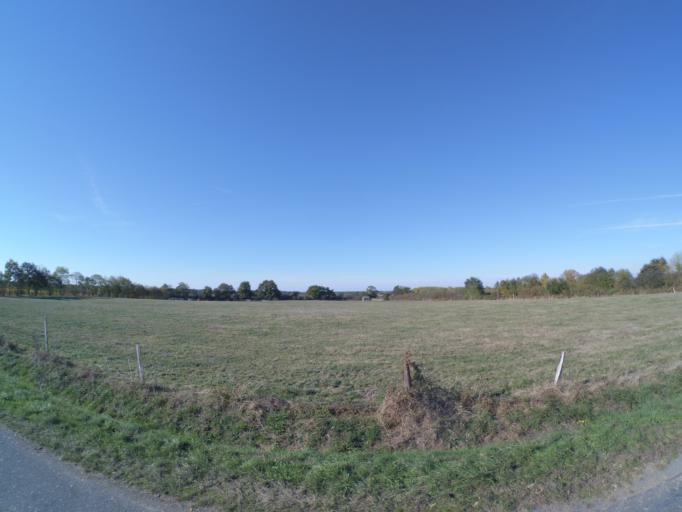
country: FR
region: Pays de la Loire
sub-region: Departement de la Loire-Atlantique
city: Saint-Lumine-de-Clisson
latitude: 47.0717
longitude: -1.3302
